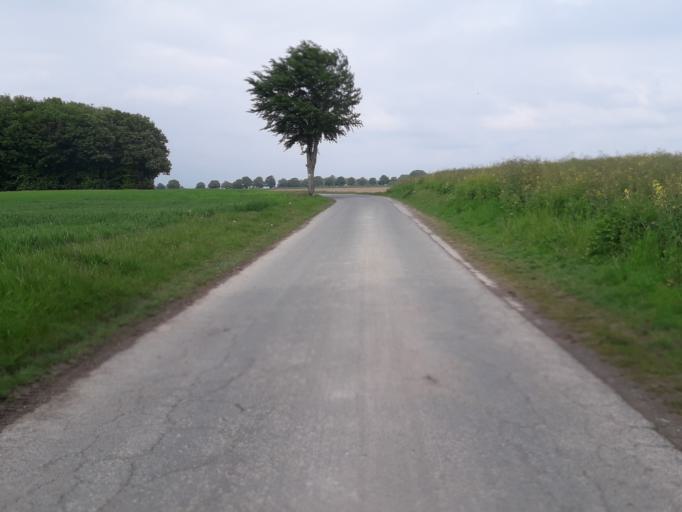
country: DE
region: North Rhine-Westphalia
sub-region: Regierungsbezirk Detmold
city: Paderborn
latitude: 51.6797
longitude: 8.7555
